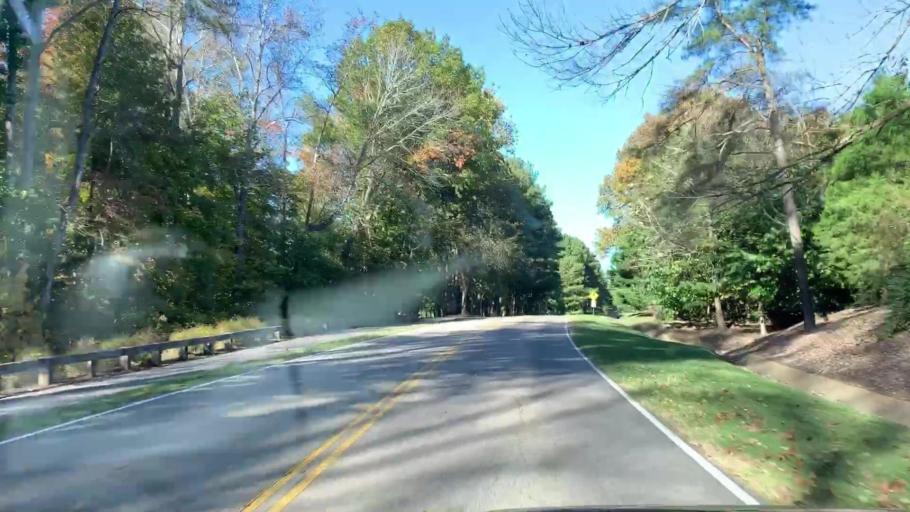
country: US
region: Virginia
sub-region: City of Williamsburg
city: Williamsburg
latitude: 37.2396
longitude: -76.6811
